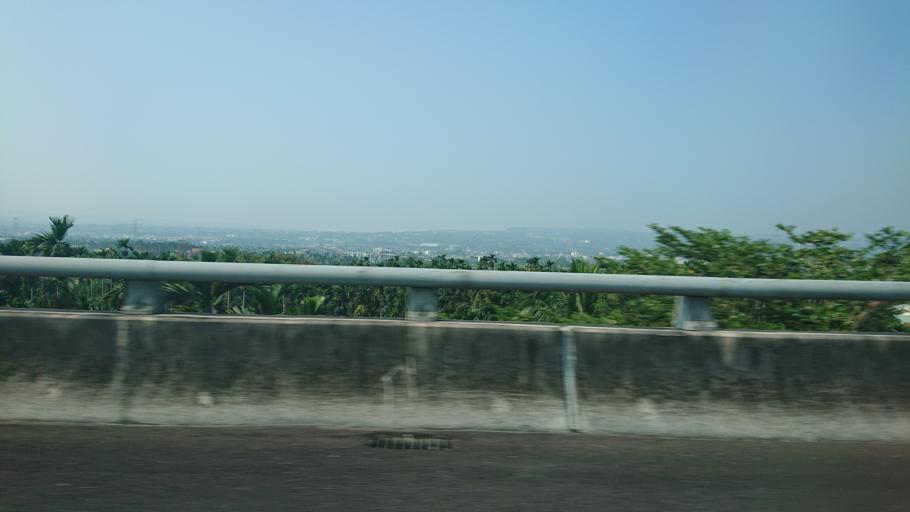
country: TW
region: Taiwan
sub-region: Nantou
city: Nantou
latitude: 23.8963
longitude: 120.7105
